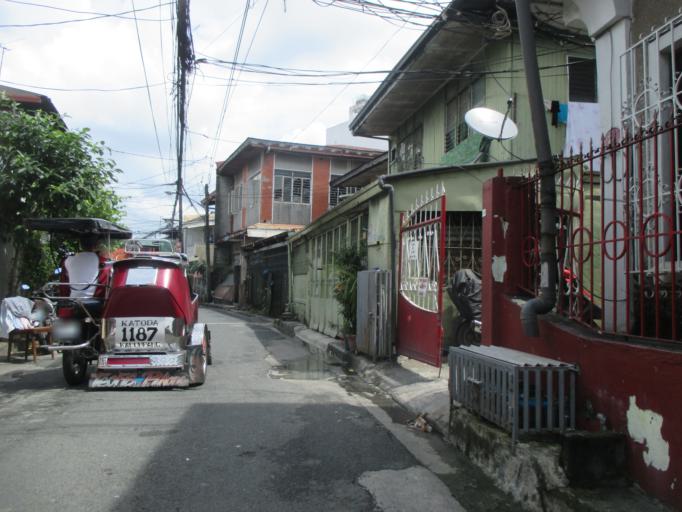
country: PH
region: Metro Manila
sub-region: Marikina
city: Calumpang
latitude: 14.6249
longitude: 121.0966
